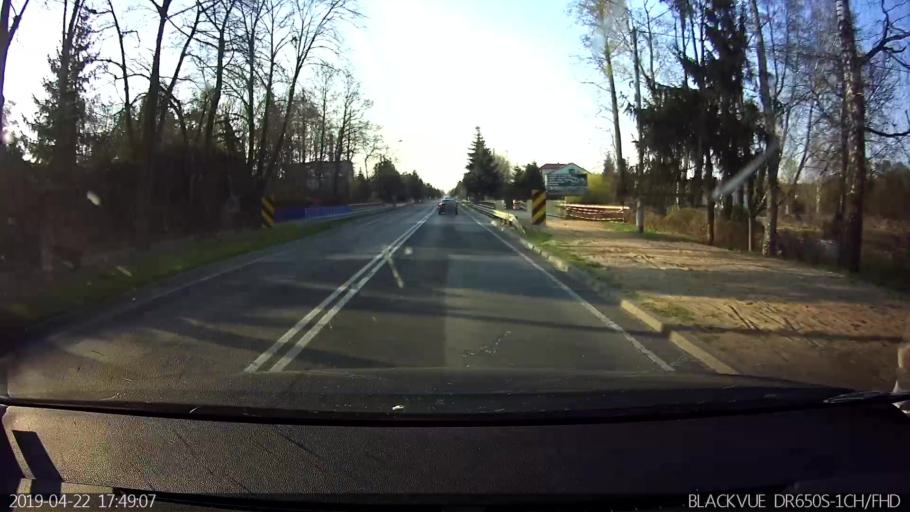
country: PL
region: Masovian Voivodeship
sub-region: Powiat wegrowski
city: Wegrow
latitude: 52.4111
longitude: 22.0107
